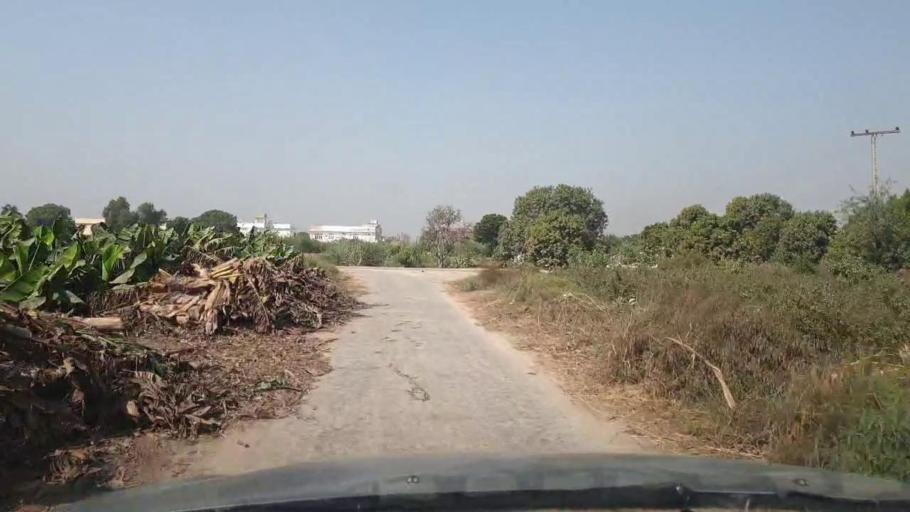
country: PK
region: Sindh
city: Tando Jam
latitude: 25.3646
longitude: 68.5068
